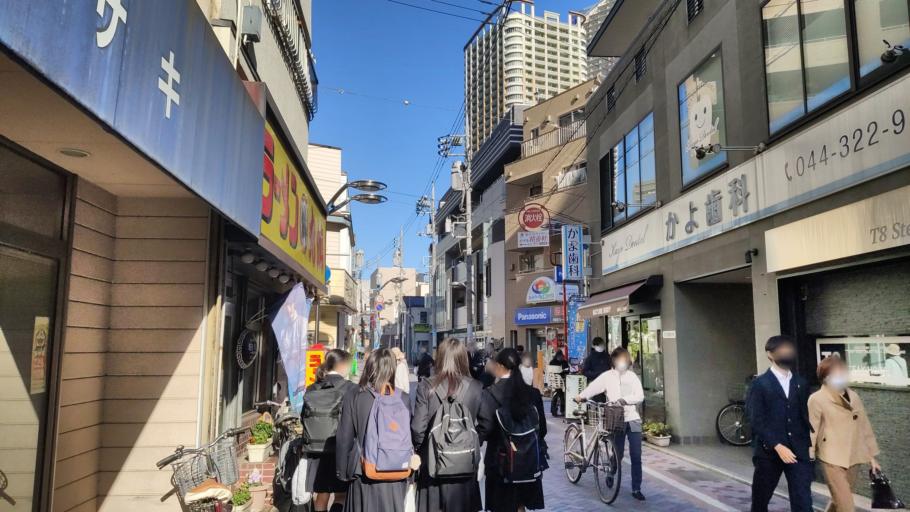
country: JP
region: Kanagawa
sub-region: Kawasaki-shi
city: Kawasaki
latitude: 35.5732
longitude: 139.6570
